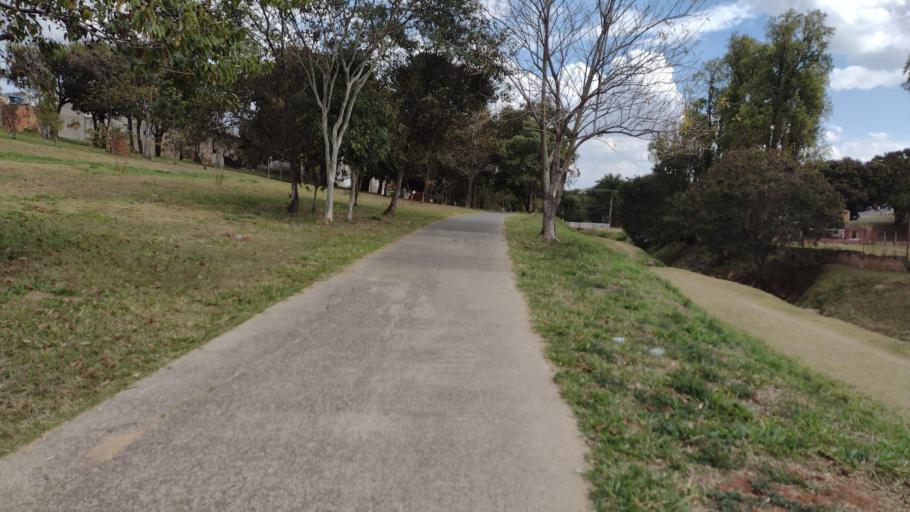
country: BR
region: Sao Paulo
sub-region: Sorocaba
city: Sorocaba
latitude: -23.4601
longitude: -47.4711
